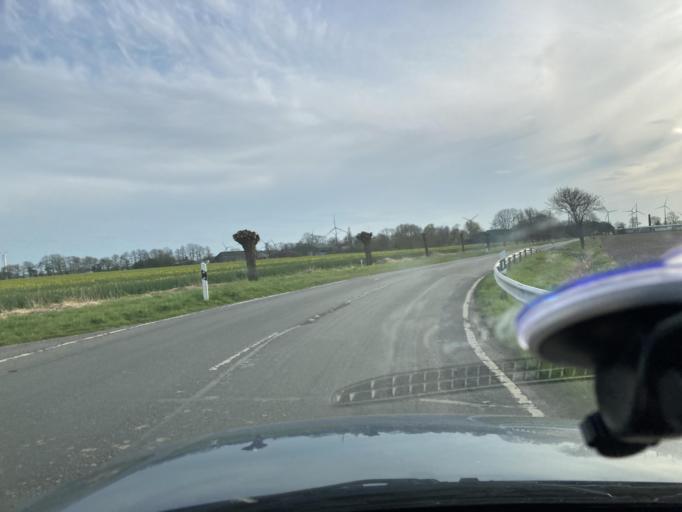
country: DE
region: Schleswig-Holstein
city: Schulp
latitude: 54.2473
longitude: 8.9436
